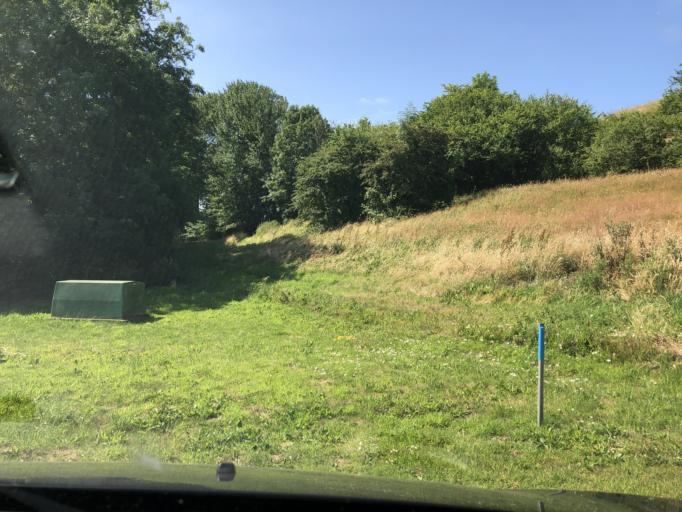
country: DK
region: South Denmark
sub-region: AEro Kommune
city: AEroskobing
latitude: 54.9213
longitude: 10.2827
